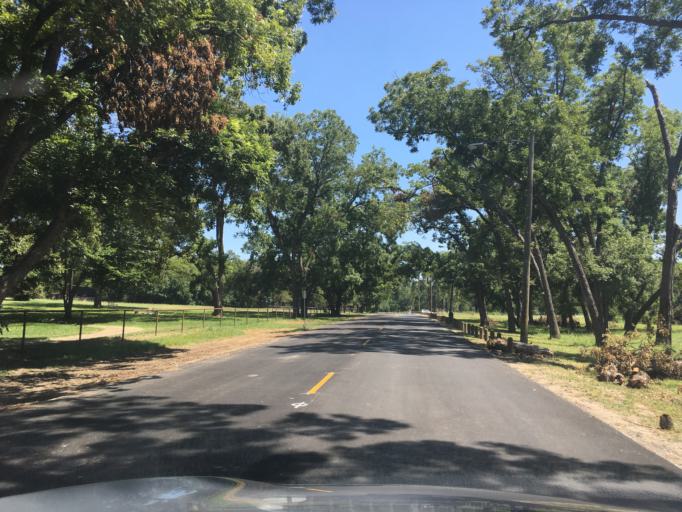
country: US
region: Texas
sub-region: Dallas County
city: Highland Park
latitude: 32.8624
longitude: -96.7300
